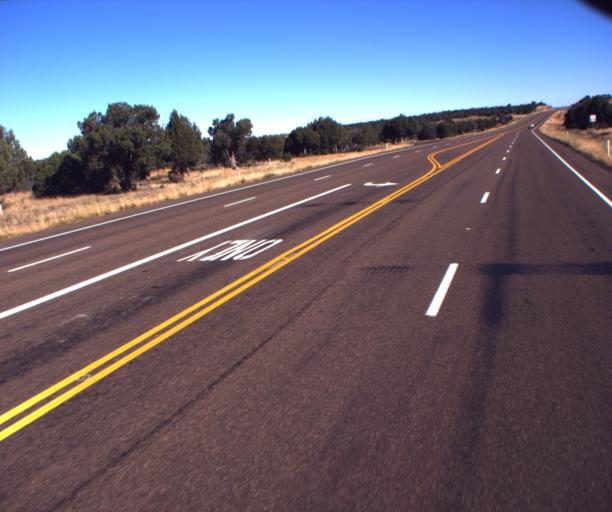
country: US
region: Arizona
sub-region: Navajo County
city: White Mountain Lake
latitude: 34.3592
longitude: -110.0532
